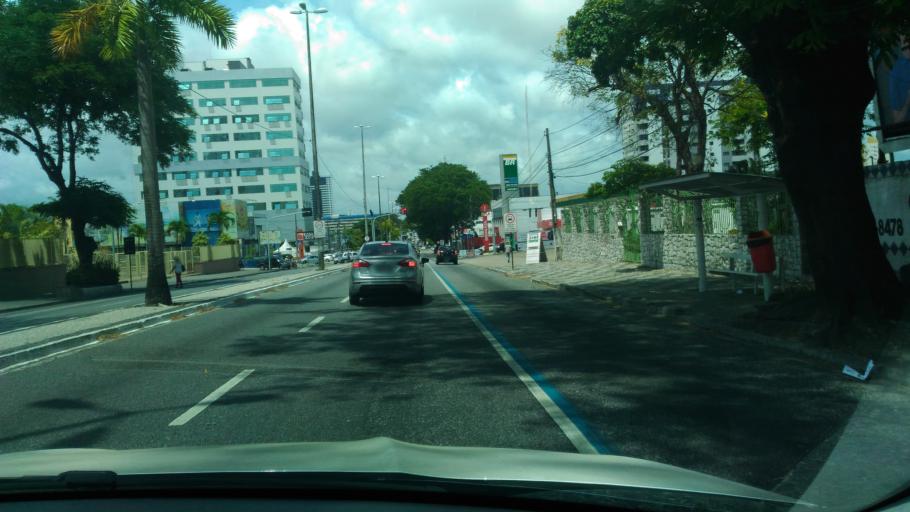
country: BR
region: Paraiba
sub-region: Joao Pessoa
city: Joao Pessoa
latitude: -7.1196
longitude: -34.8524
